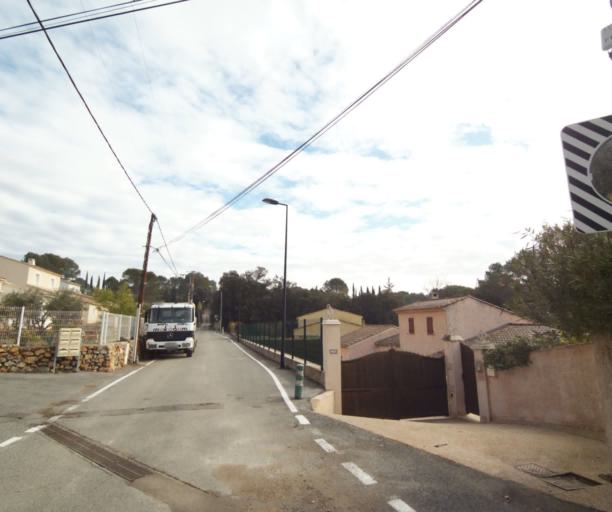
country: FR
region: Provence-Alpes-Cote d'Azur
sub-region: Departement du Var
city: Trans-en-Provence
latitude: 43.5023
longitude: 6.4973
